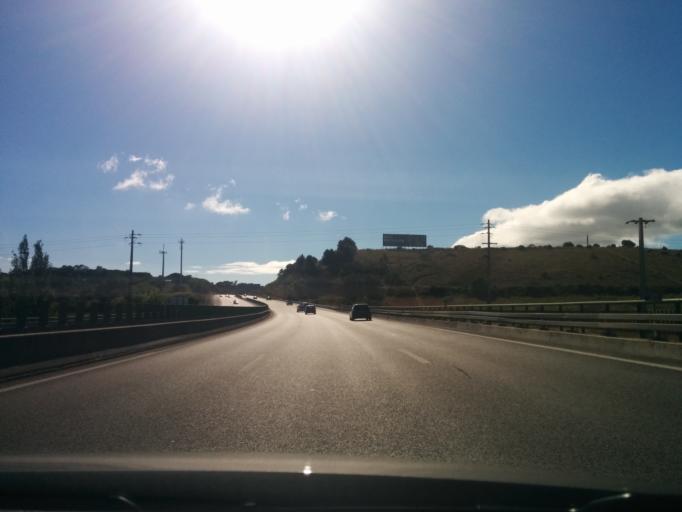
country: PT
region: Lisbon
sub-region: Cascais
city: Parede
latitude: 38.7188
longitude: -9.3669
